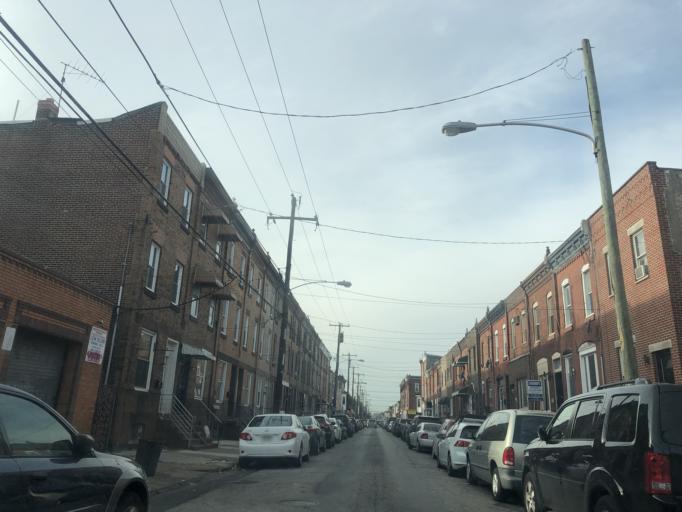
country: US
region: Pennsylvania
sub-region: Philadelphia County
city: Philadelphia
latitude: 39.9287
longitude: -75.1739
